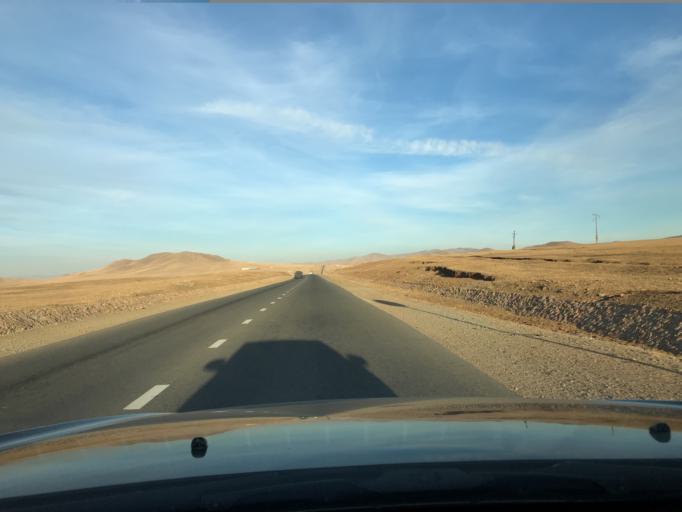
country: MN
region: Central Aimak
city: Arhust
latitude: 47.7853
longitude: 107.4592
